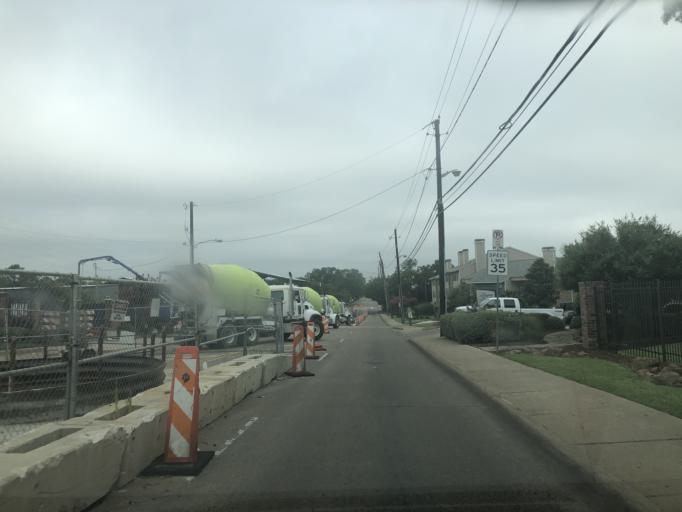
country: US
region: Texas
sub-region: Dallas County
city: Farmers Branch
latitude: 32.8665
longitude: -96.8674
